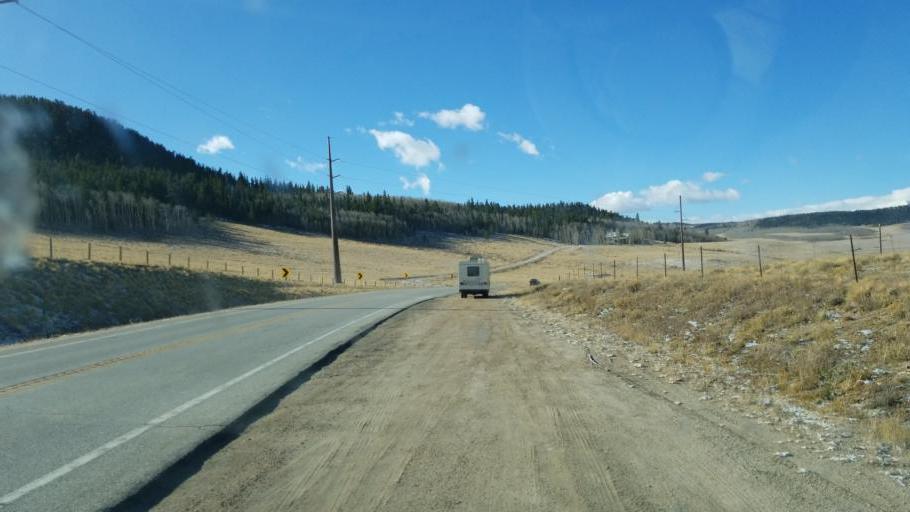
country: US
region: Colorado
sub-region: Park County
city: Fairplay
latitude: 39.2809
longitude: -105.9153
